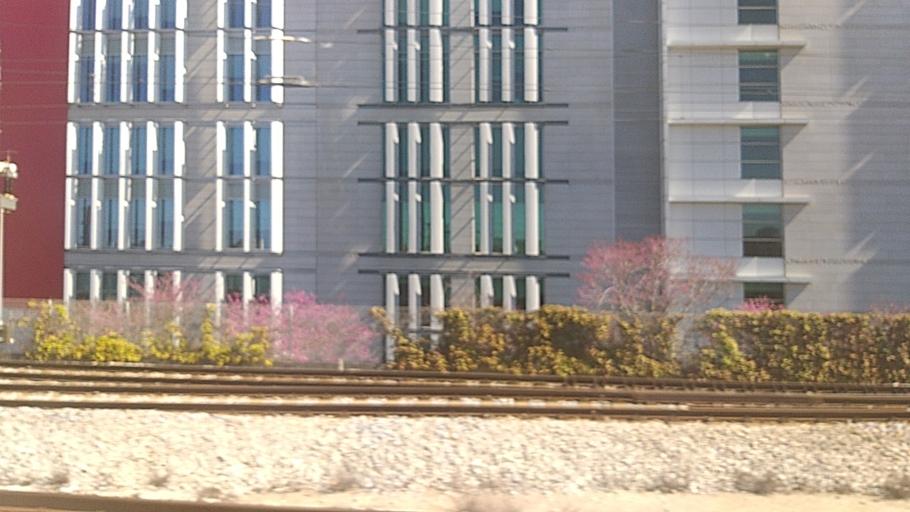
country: PT
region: Lisbon
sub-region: Loures
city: Moscavide
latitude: 38.7639
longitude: -9.0995
